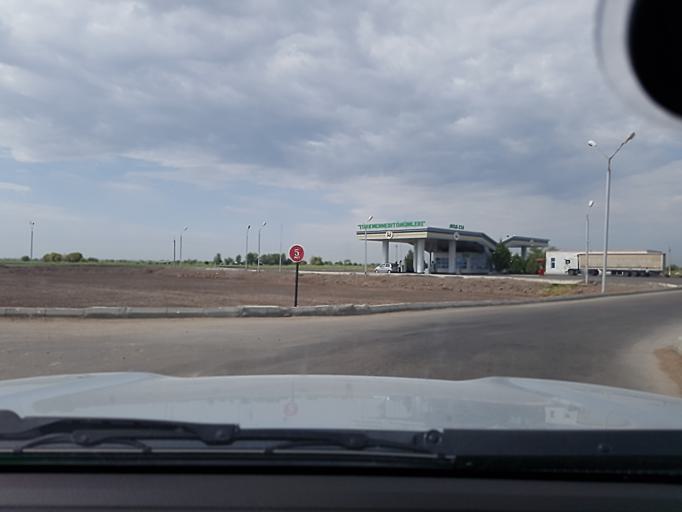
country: TM
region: Dasoguz
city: Dasoguz
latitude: 41.9050
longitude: 59.9353
